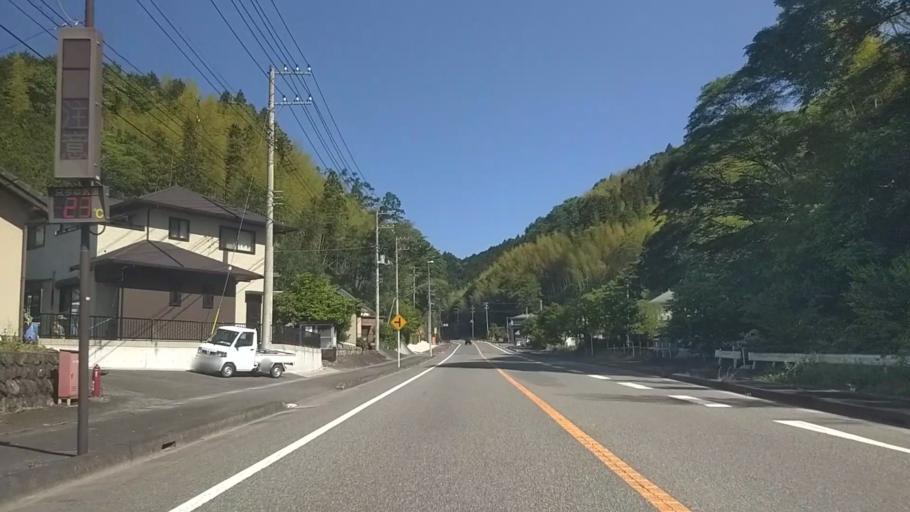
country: JP
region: Shizuoka
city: Fujinomiya
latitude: 35.2648
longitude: 138.4621
